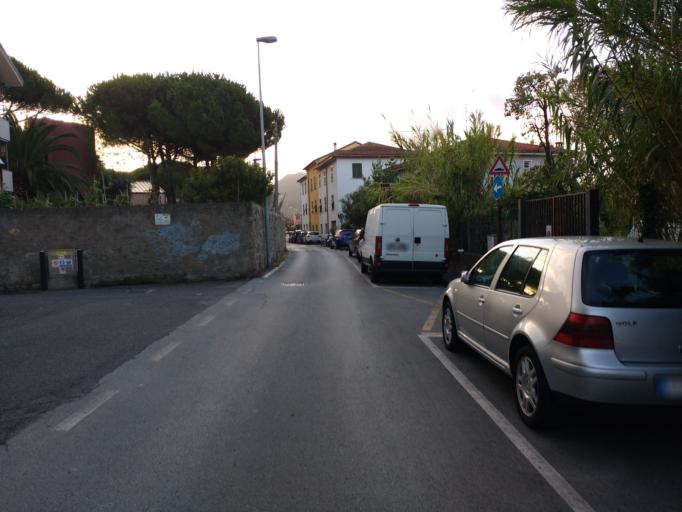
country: IT
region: Liguria
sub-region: Provincia di Genova
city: Sestri Levante
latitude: 44.2710
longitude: 9.4116
